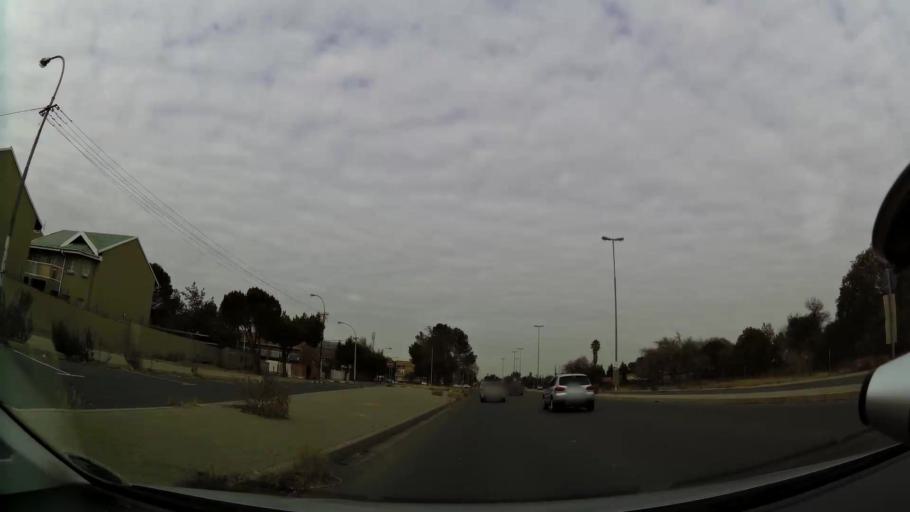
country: ZA
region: Orange Free State
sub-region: Mangaung Metropolitan Municipality
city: Bloemfontein
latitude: -29.1195
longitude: 26.1996
